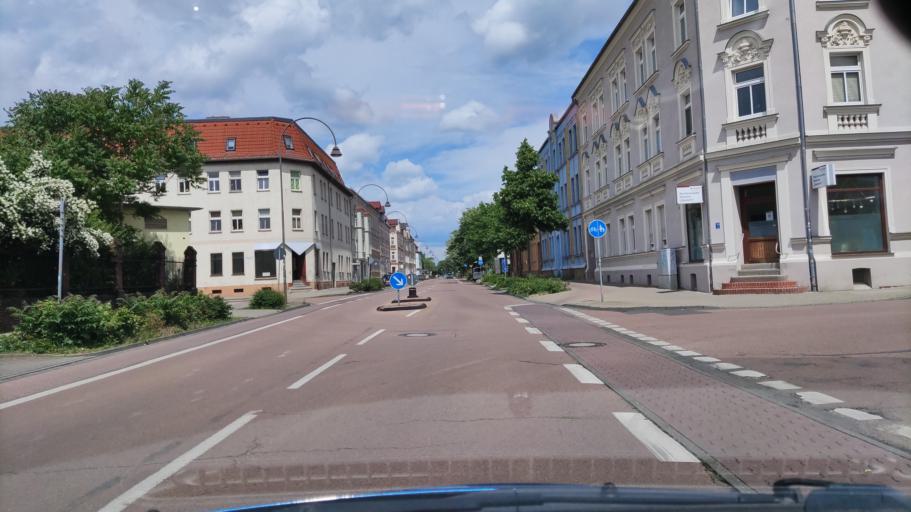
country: DE
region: Saxony-Anhalt
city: Wittenburg
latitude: 51.8708
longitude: 12.6534
